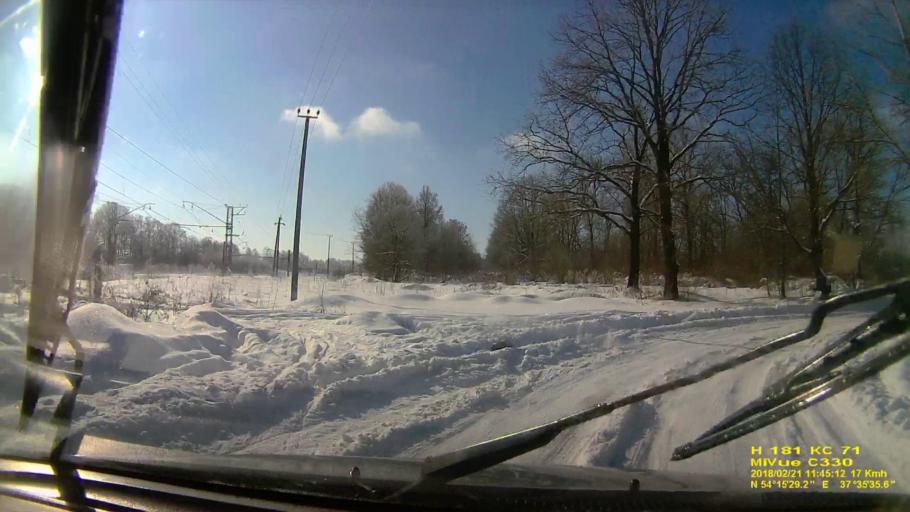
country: RU
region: Tula
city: Gorelki
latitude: 54.2581
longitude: 37.5932
